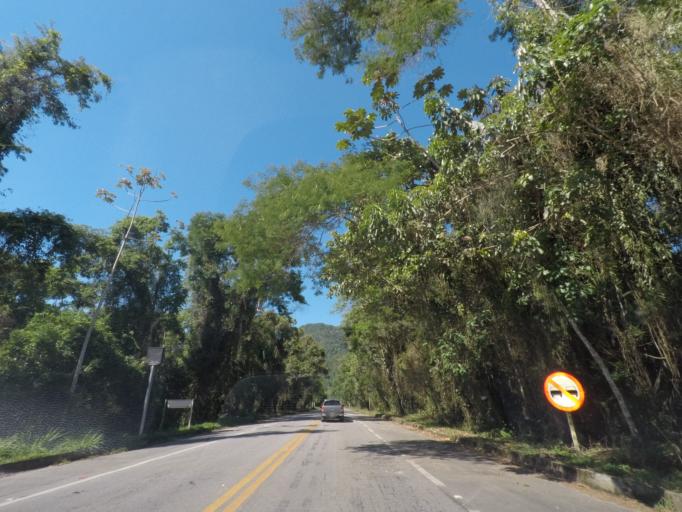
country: BR
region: Sao Paulo
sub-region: Ubatuba
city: Ubatuba
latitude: -23.3452
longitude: -44.9419
